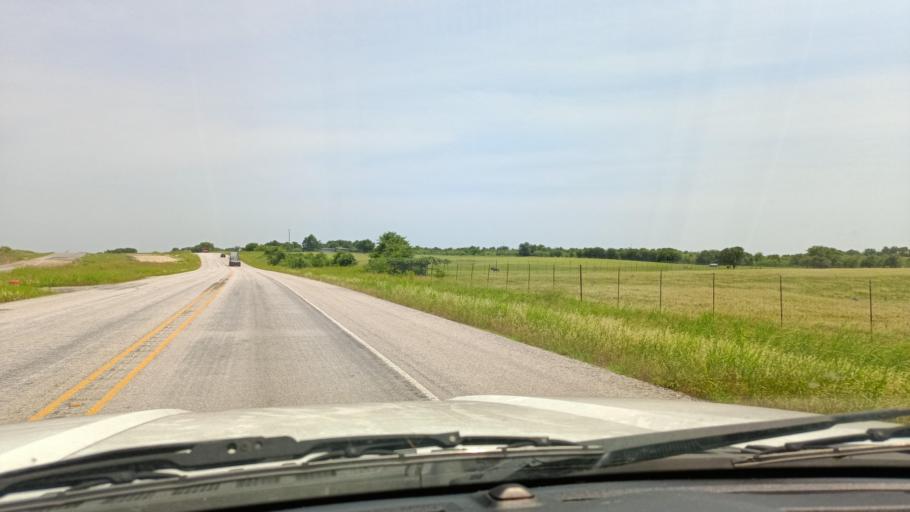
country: US
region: Texas
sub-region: Bell County
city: Rogers
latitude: 30.9552
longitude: -97.2568
